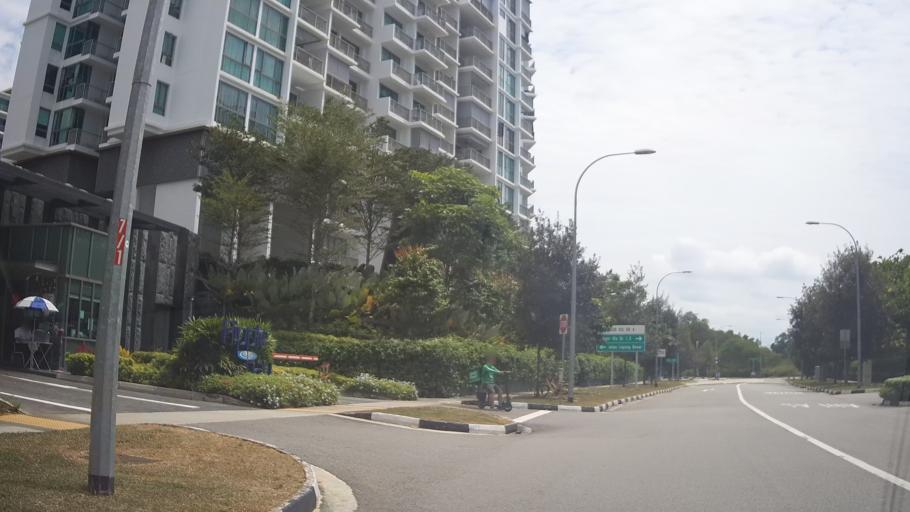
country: MY
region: Johor
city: Kampung Pasir Gudang Baru
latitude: 1.3771
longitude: 103.9604
